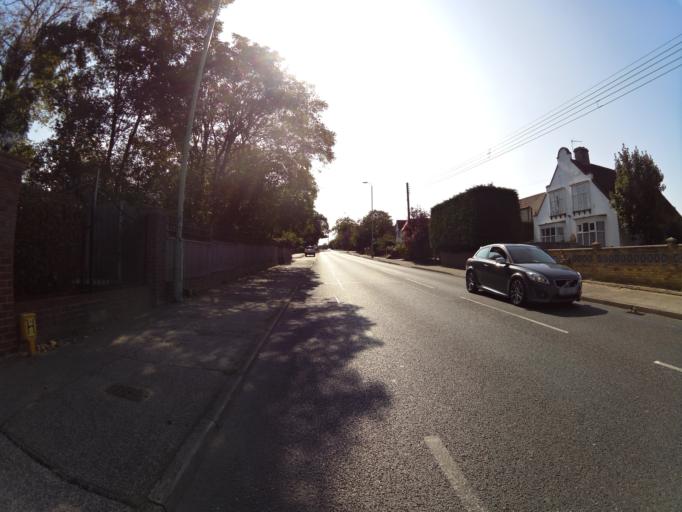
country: GB
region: England
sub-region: Suffolk
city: Lowestoft
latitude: 52.4673
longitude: 1.7080
